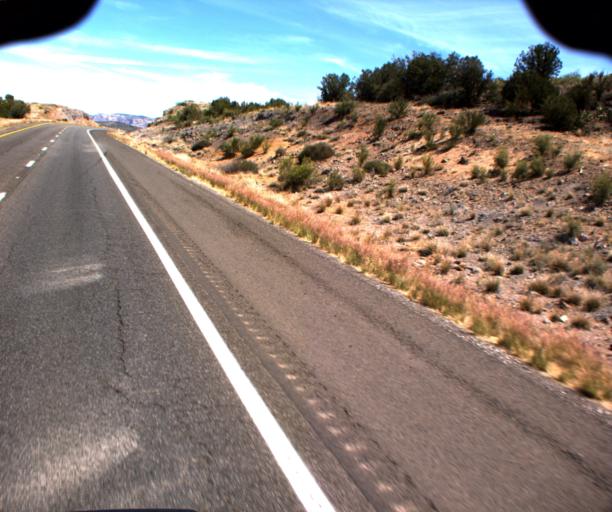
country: US
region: Arizona
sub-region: Yavapai County
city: Cornville
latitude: 34.8024
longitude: -111.9113
